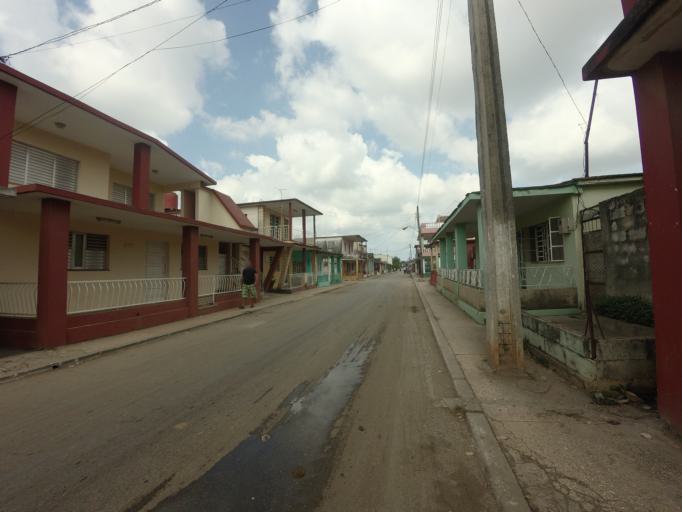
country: CU
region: Artemisa
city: Bauta
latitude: 22.9808
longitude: -82.5503
